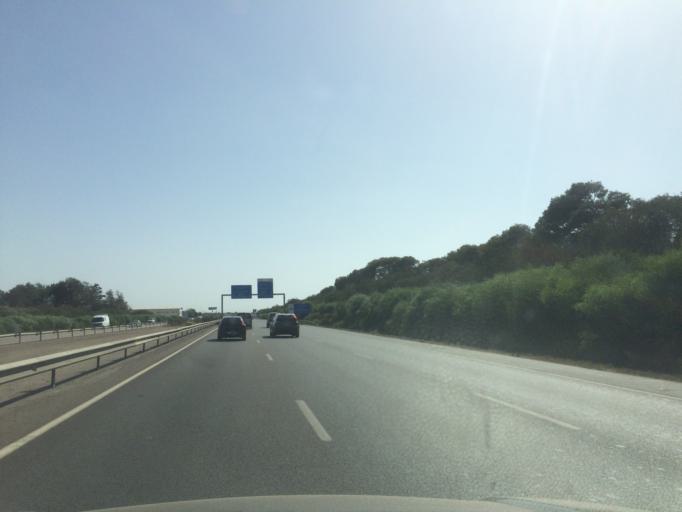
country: MA
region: Rabat-Sale-Zemmour-Zaer
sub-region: Skhirate-Temara
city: Temara
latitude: 33.9397
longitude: -6.9290
